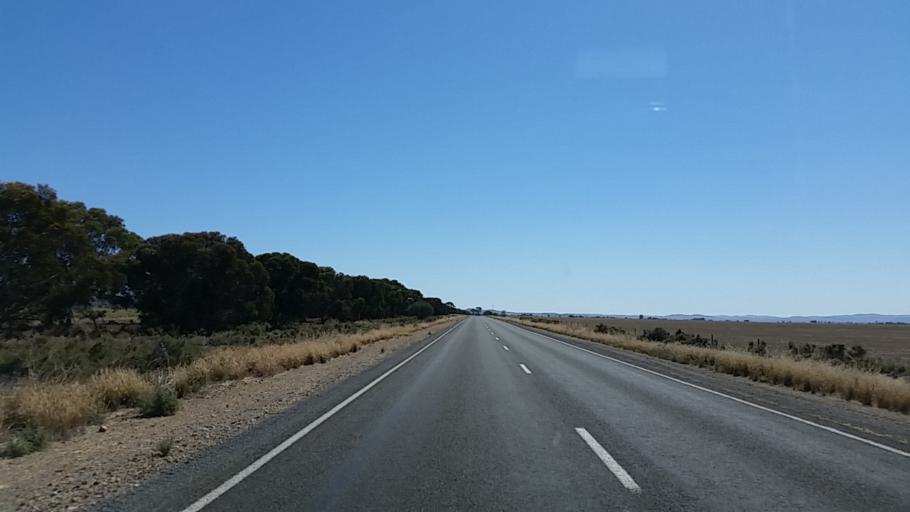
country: AU
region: South Australia
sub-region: Peterborough
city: Peterborough
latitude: -32.7563
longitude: 138.6467
